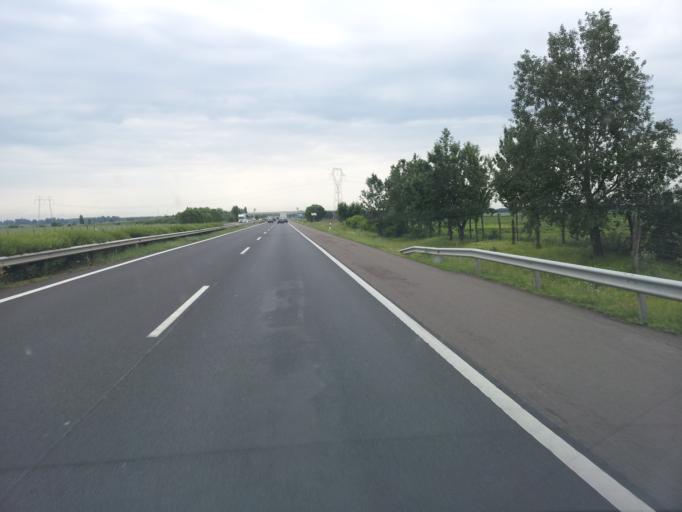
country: HU
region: Heves
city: Adacs
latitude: 47.7189
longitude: 19.9942
